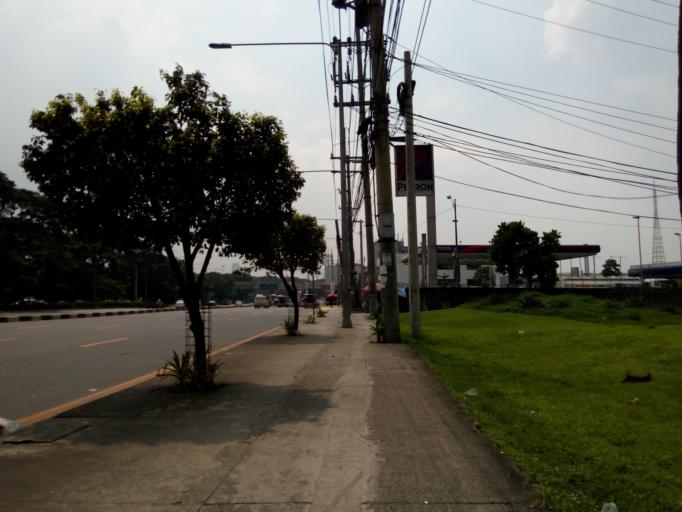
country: PH
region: Metro Manila
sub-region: Quezon City
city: Quezon City
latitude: 14.6552
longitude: 121.0544
